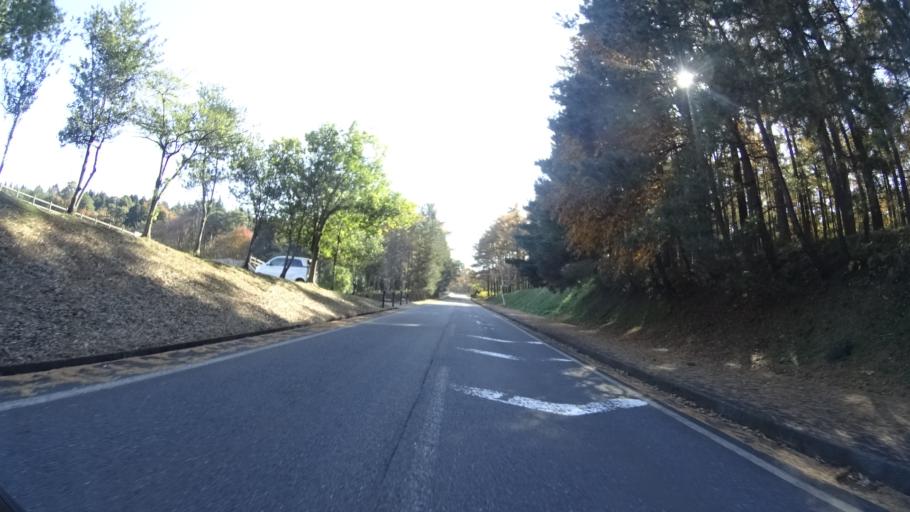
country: JP
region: Niigata
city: Itoigawa
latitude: 37.0226
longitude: 137.8667
